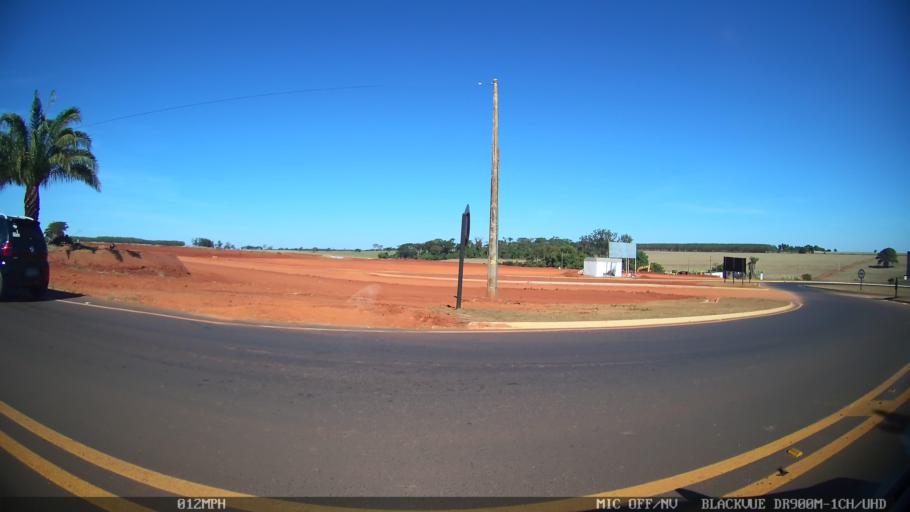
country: BR
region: Sao Paulo
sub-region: Olimpia
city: Olimpia
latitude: -20.7352
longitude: -48.8760
